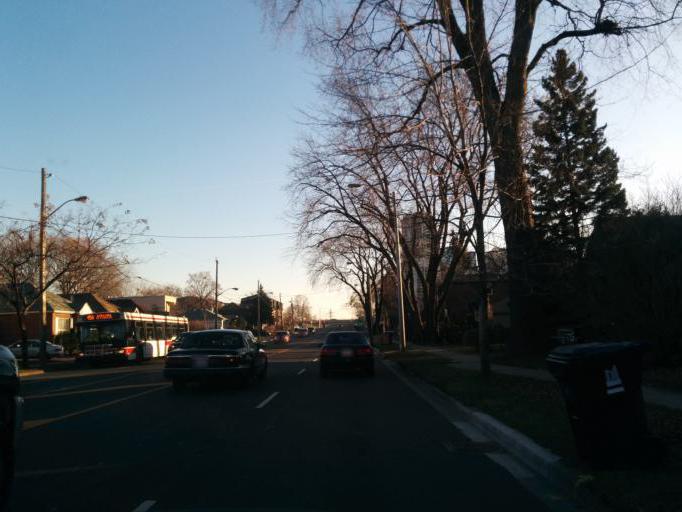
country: CA
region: Ontario
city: Etobicoke
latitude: 43.6447
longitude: -79.5366
